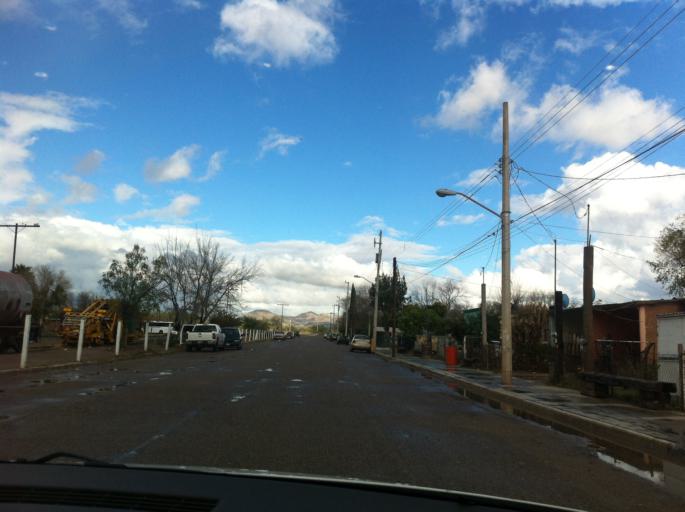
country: MX
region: Sonora
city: Magdalena de Kino
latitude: 30.6358
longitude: -110.9677
